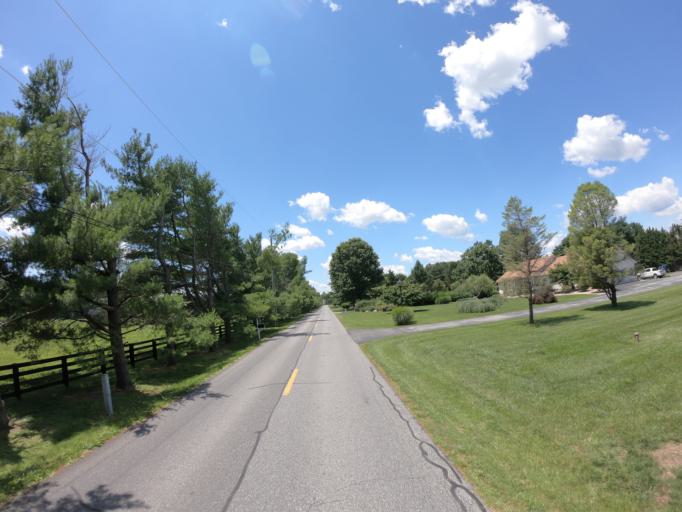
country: US
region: Delaware
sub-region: New Castle County
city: Middletown
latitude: 39.4806
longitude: -75.7439
